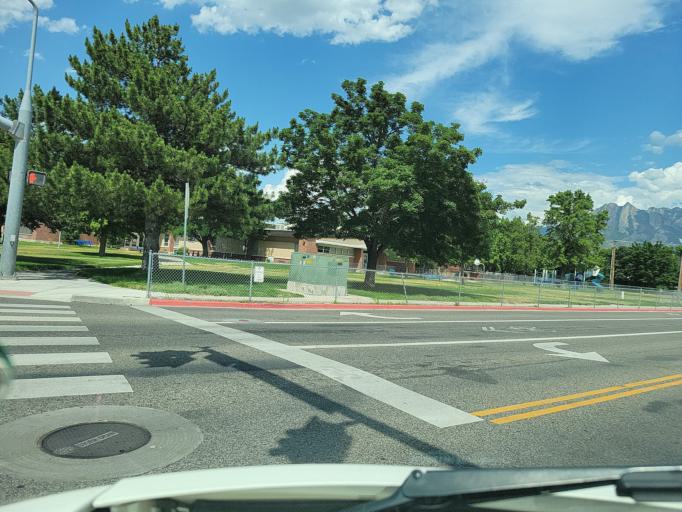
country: US
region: Utah
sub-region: Salt Lake County
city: Murray
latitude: 40.6423
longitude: -111.8829
